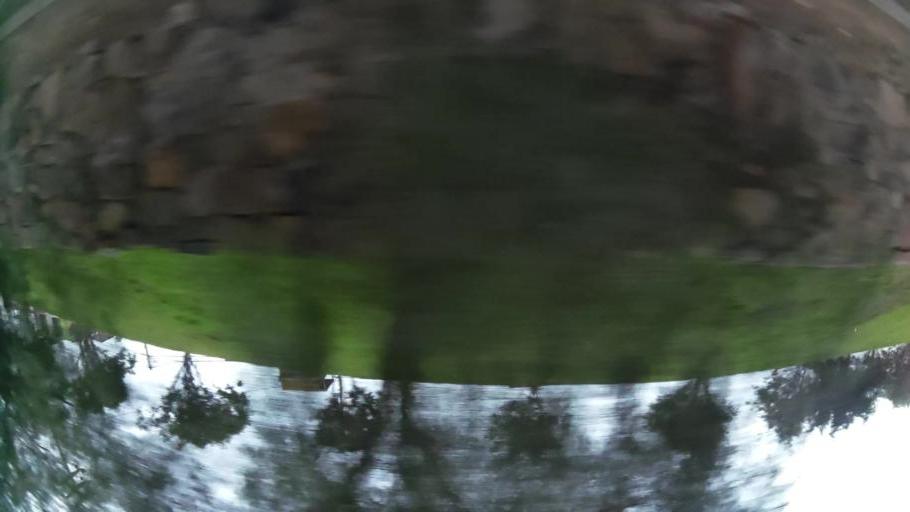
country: PE
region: Lima
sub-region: Lima
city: La Molina
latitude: -12.1120
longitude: -76.9419
